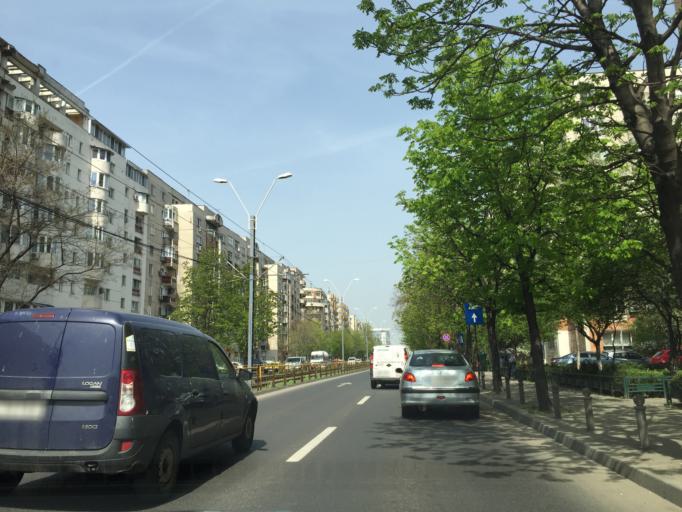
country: RO
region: Ilfov
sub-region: Comuna Chiajna
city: Rosu
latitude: 44.4372
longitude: 26.0353
